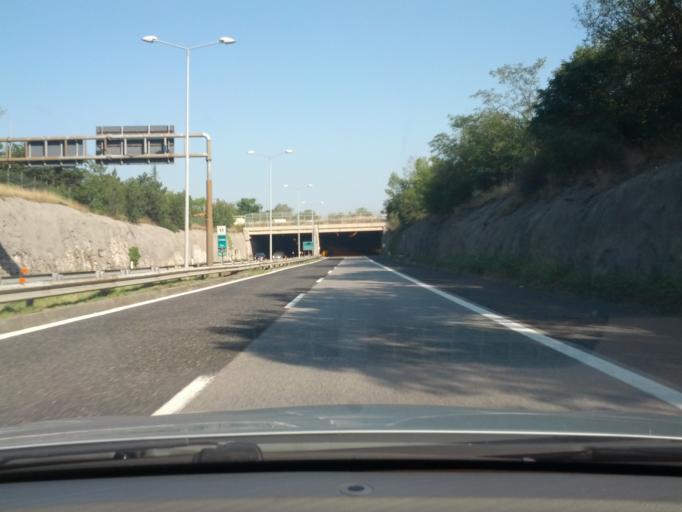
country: IT
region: Friuli Venezia Giulia
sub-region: Provincia di Trieste
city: Prosecco-Contovello
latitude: 45.7056
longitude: 13.7473
